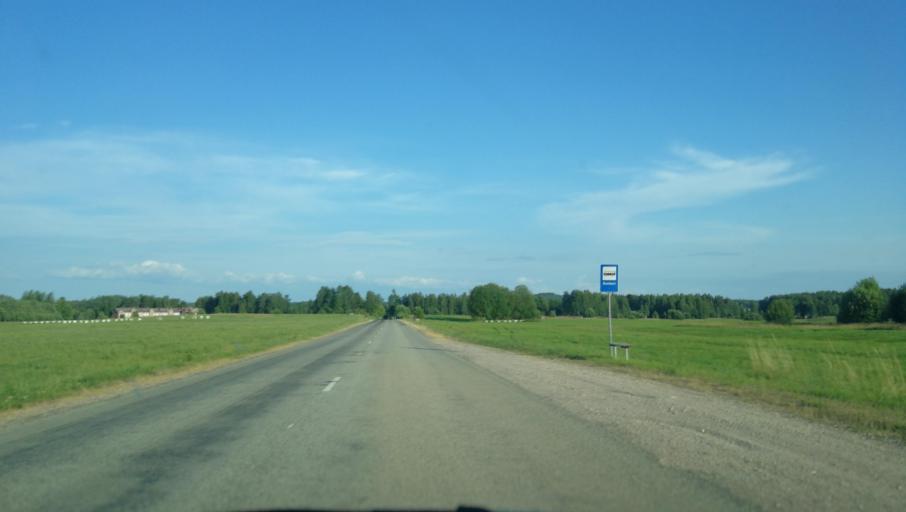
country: LV
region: Cesu Rajons
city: Cesis
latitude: 57.2799
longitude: 25.3182
